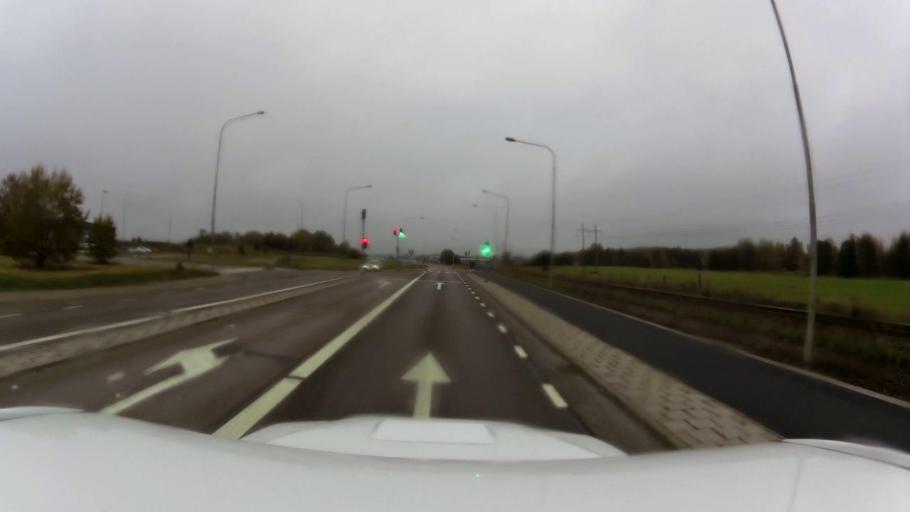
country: SE
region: OEstergoetland
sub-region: Linkopings Kommun
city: Linkoping
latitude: 58.4001
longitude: 15.6747
